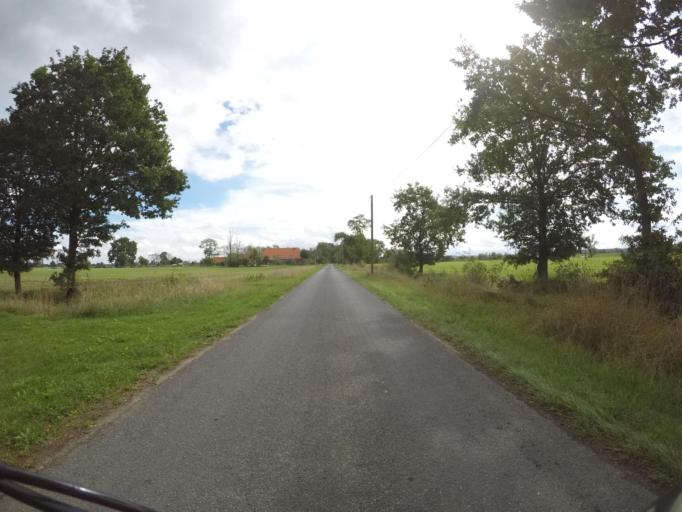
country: DE
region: Lower Saxony
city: Neu Darchau
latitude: 53.2594
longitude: 10.8576
